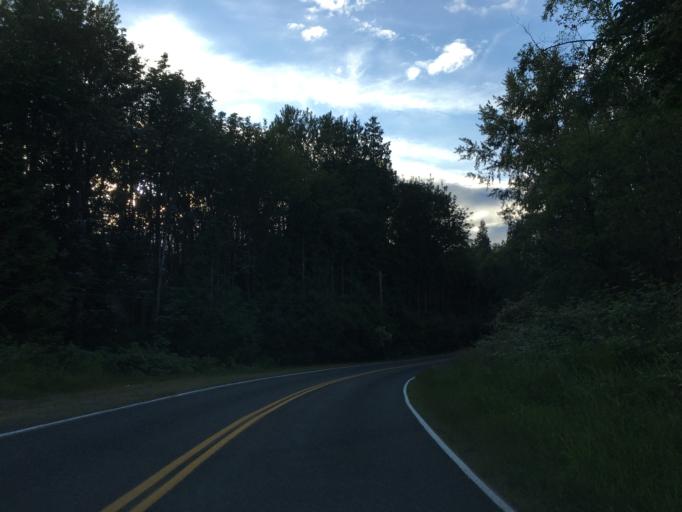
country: CA
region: British Columbia
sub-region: Greater Vancouver Regional District
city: White Rock
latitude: 48.9409
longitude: -122.8185
